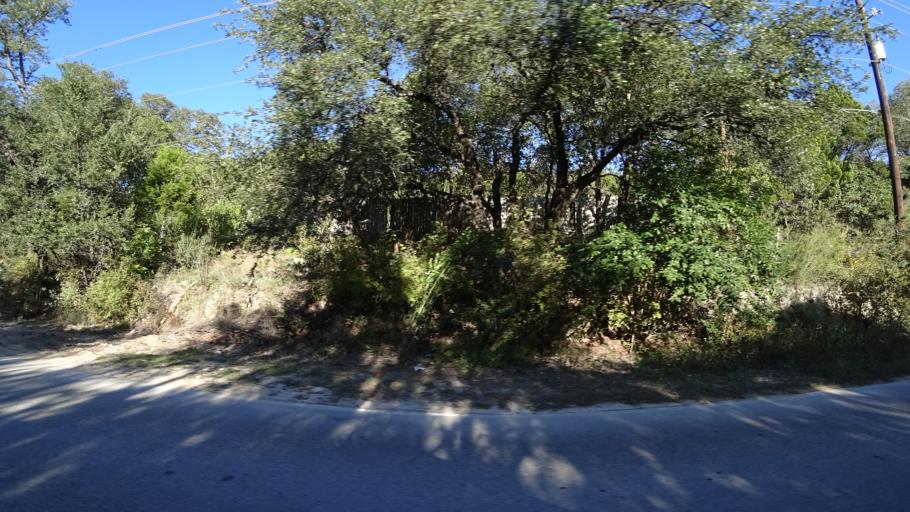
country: US
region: Texas
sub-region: Travis County
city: West Lake Hills
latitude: 30.3637
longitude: -97.8013
